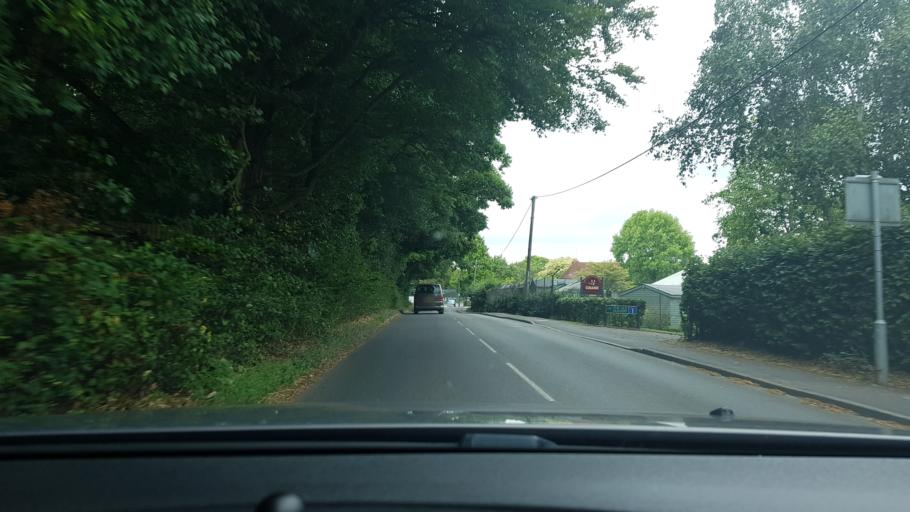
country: GB
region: England
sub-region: West Berkshire
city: Hermitage
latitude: 51.4523
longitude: -1.2794
